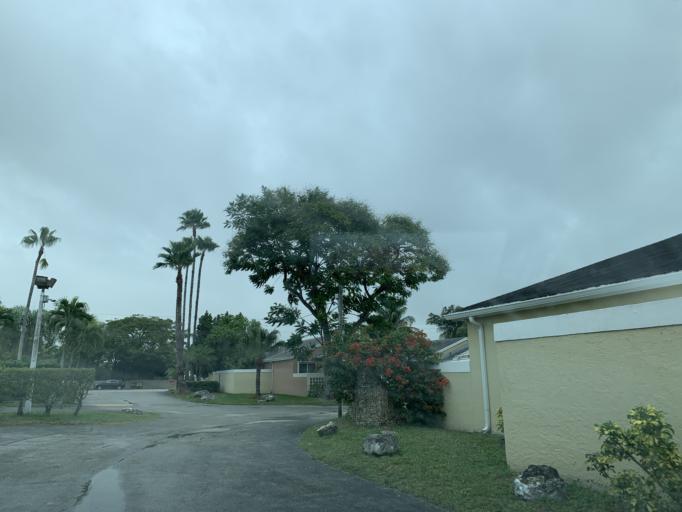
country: US
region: Florida
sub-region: Miami-Dade County
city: Kendall West
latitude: 25.6985
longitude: -80.4354
